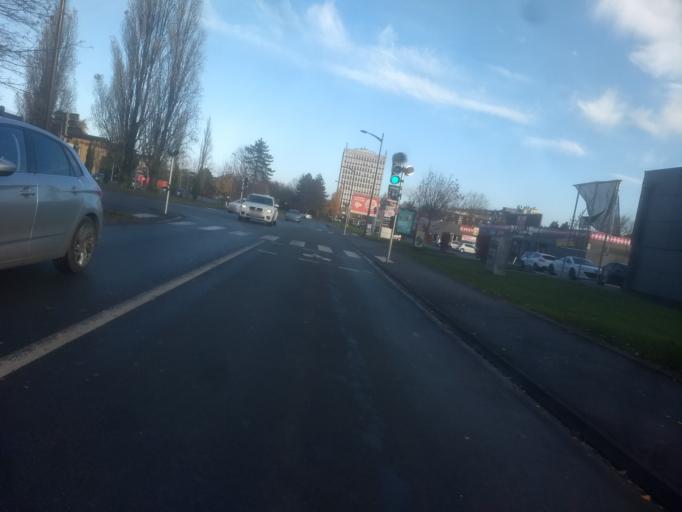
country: FR
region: Nord-Pas-de-Calais
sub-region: Departement du Pas-de-Calais
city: Anzin-Saint-Aubin
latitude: 50.2985
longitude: 2.7387
